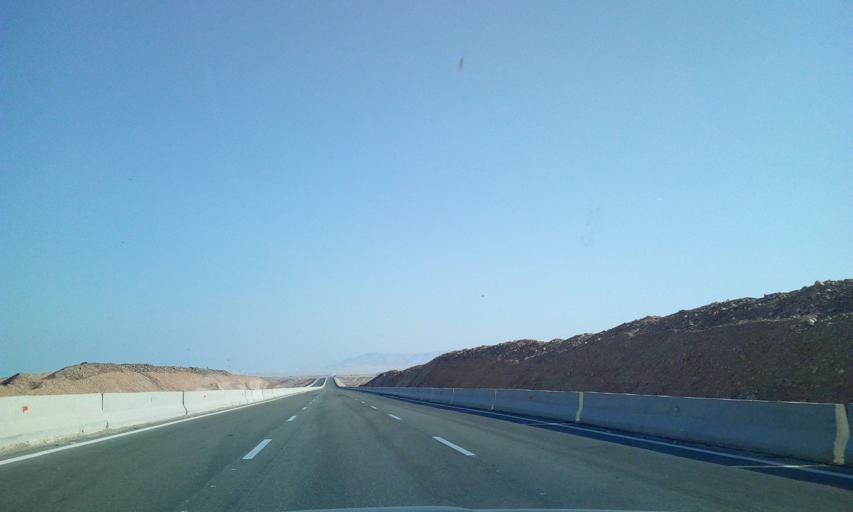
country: EG
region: As Suways
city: Ain Sukhna
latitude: 29.1898
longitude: 32.4988
